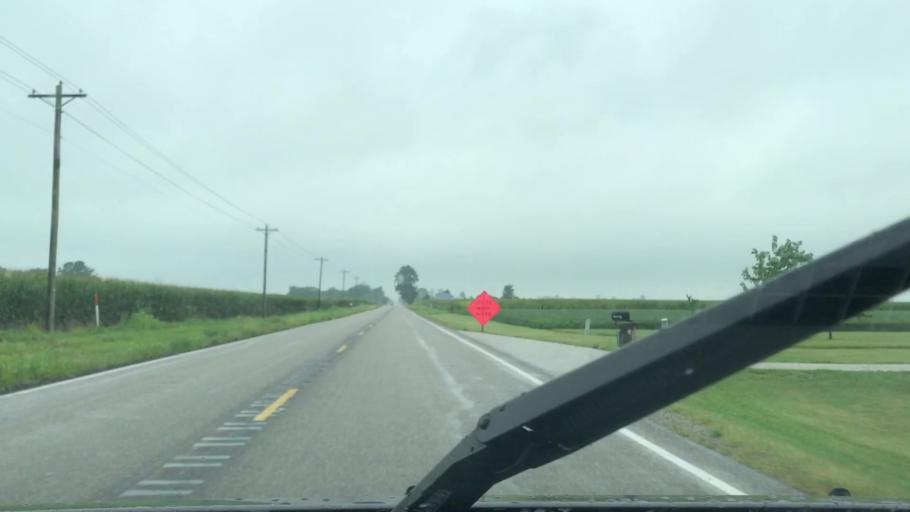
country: US
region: Indiana
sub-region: Boone County
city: Dale
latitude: 40.1268
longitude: -86.3852
